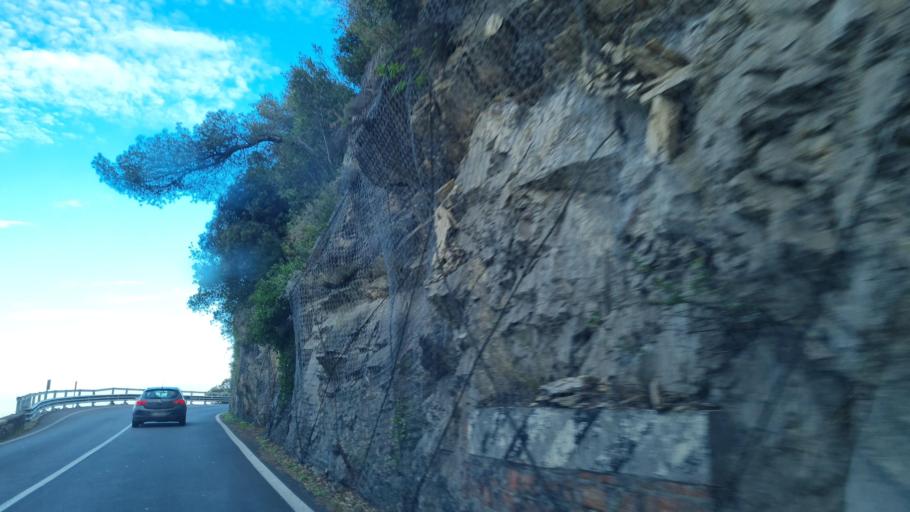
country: IT
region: Liguria
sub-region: Provincia di Savona
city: Noli
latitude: 44.1985
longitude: 8.4214
